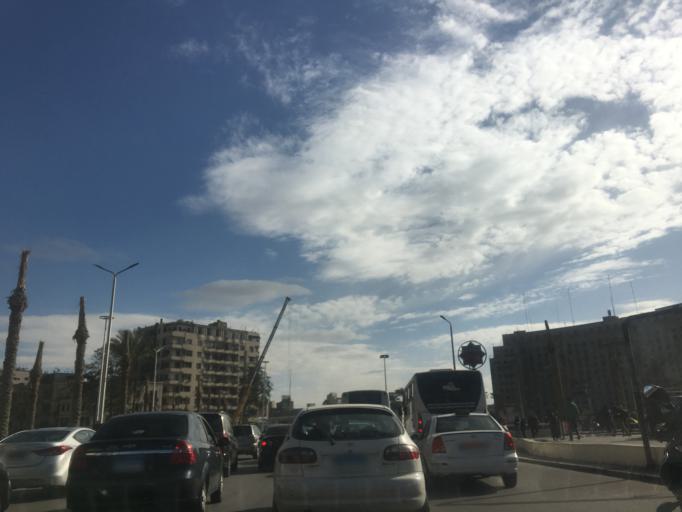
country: EG
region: Muhafazat al Qahirah
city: Cairo
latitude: 30.0456
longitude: 31.2351
